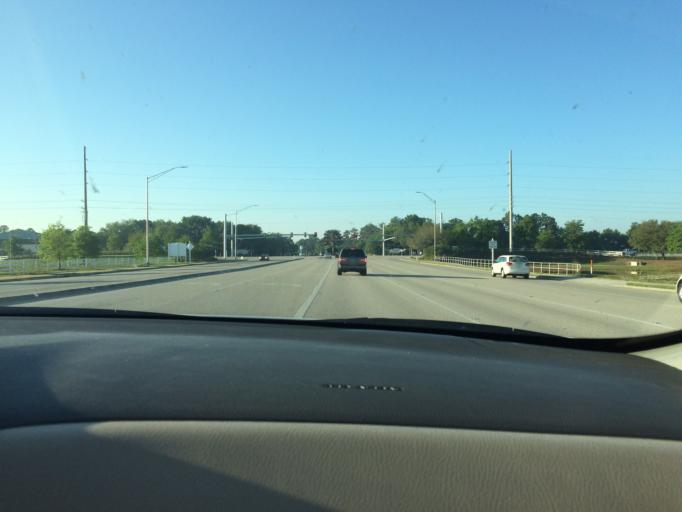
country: US
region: Florida
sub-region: Sarasota County
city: The Meadows
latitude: 27.4340
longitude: -82.4284
